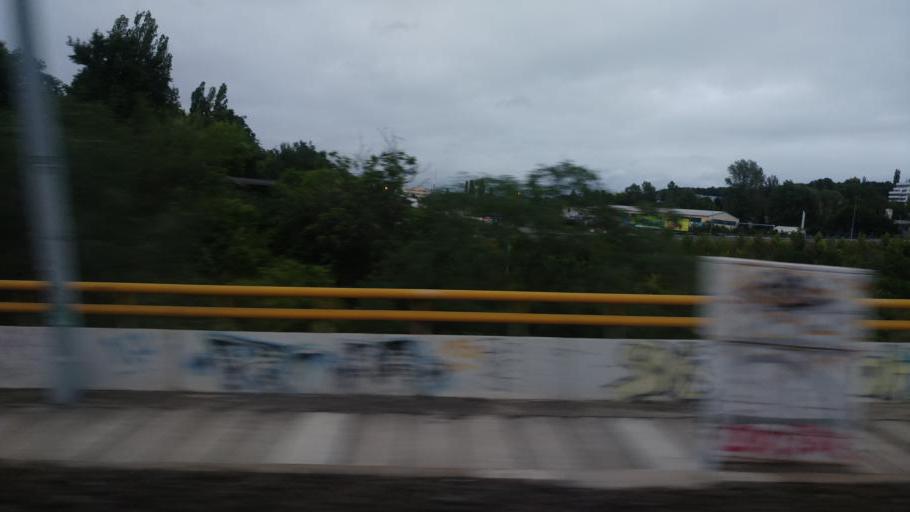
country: CZ
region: Praha
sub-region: Praha 8
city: Liben
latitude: 50.0991
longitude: 14.4733
